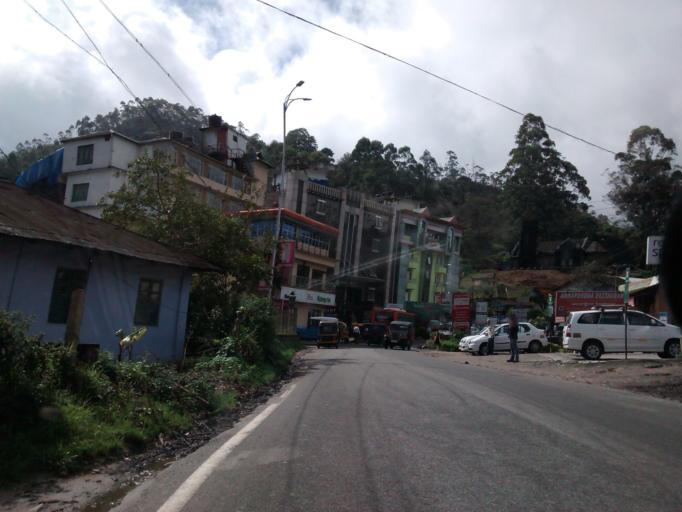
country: IN
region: Kerala
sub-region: Idukki
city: Munnar
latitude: 10.0795
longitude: 77.0621
